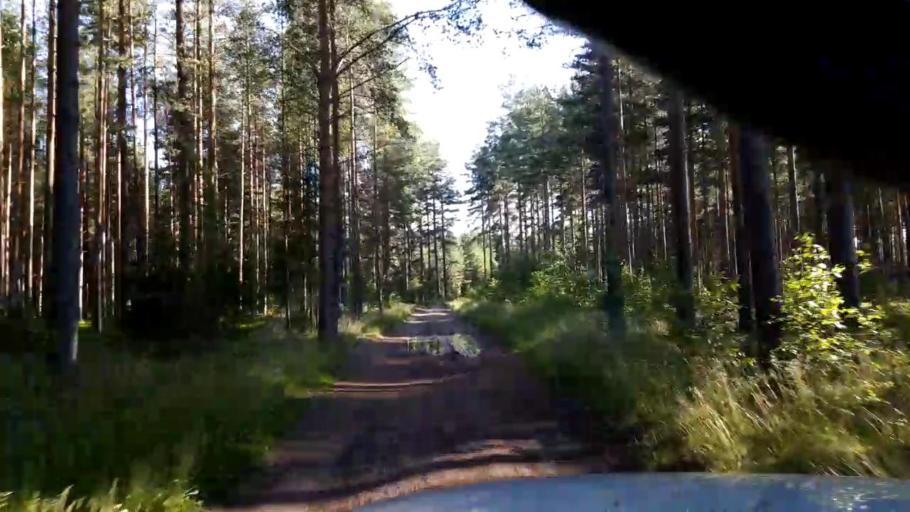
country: SE
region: Dalarna
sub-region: Borlange Kommun
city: Ornas
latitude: 60.4003
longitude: 15.5631
